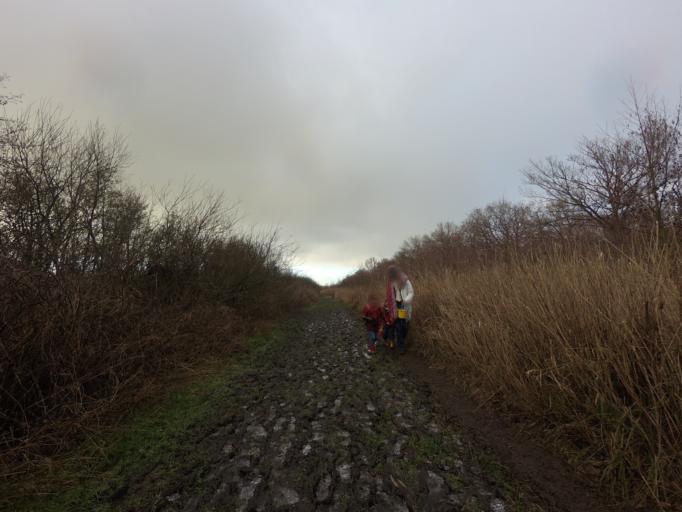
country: NL
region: North Holland
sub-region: Gemeente Weesp
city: Weesp
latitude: 52.2756
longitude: 5.0726
